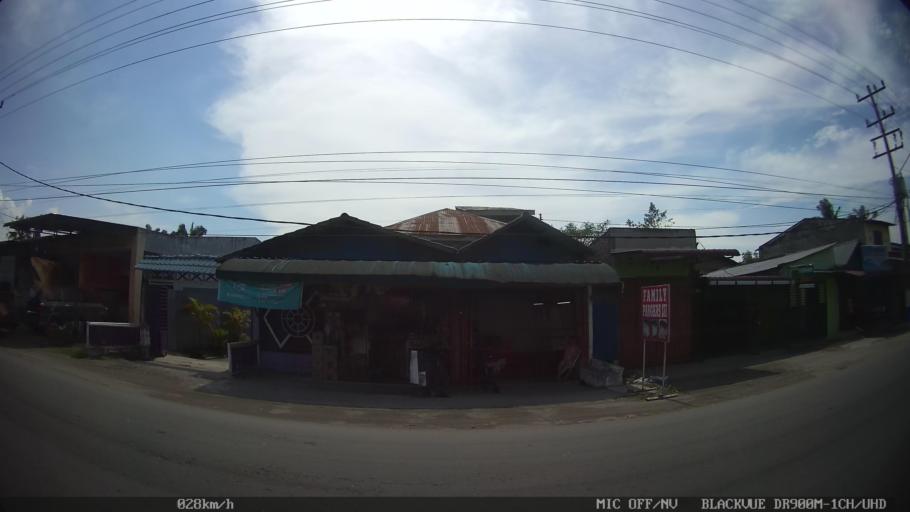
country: ID
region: North Sumatra
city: Labuhan Deli
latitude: 3.6639
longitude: 98.6560
